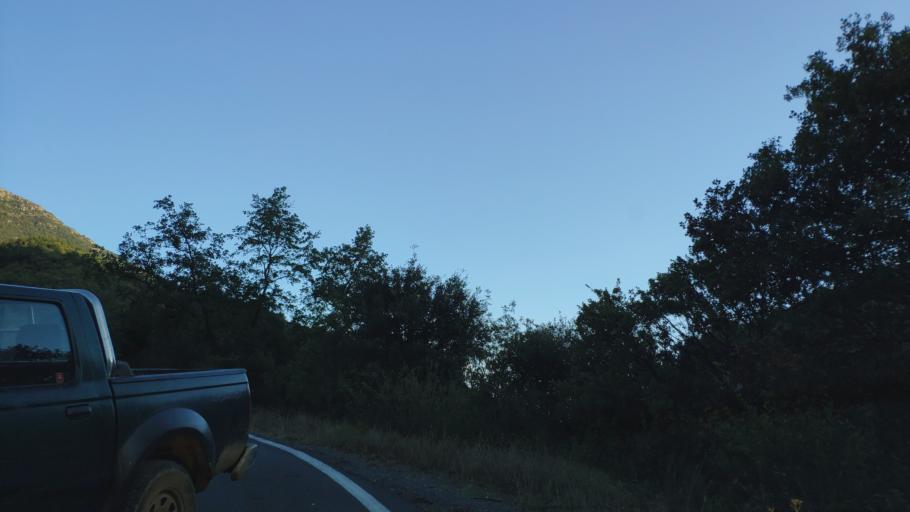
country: GR
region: Peloponnese
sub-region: Nomos Arkadias
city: Dimitsana
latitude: 37.5671
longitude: 22.0457
